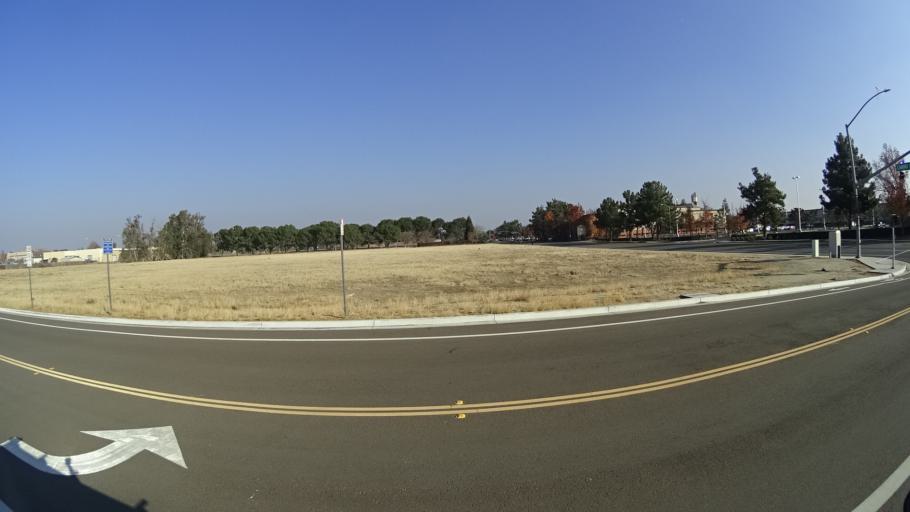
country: US
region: California
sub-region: Kern County
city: Greenacres
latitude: 35.3432
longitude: -119.1064
